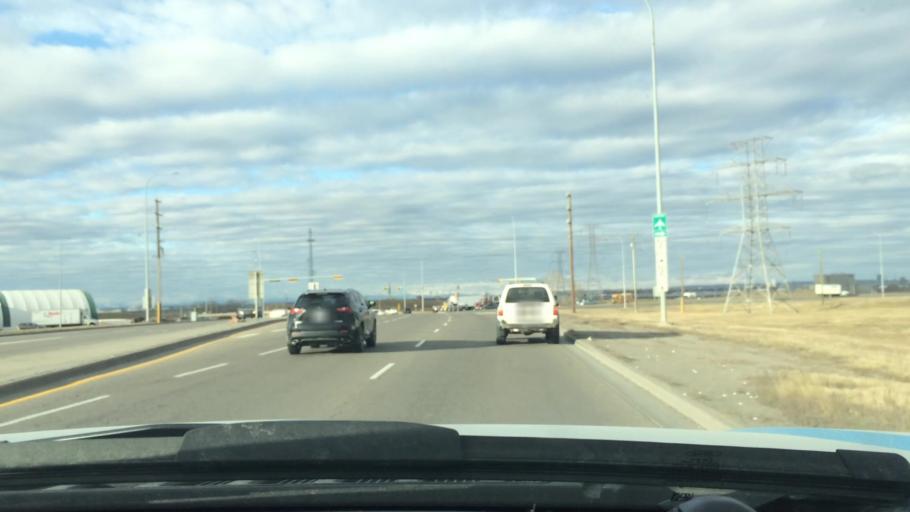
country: CA
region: Alberta
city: Calgary
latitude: 51.0155
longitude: -113.9996
